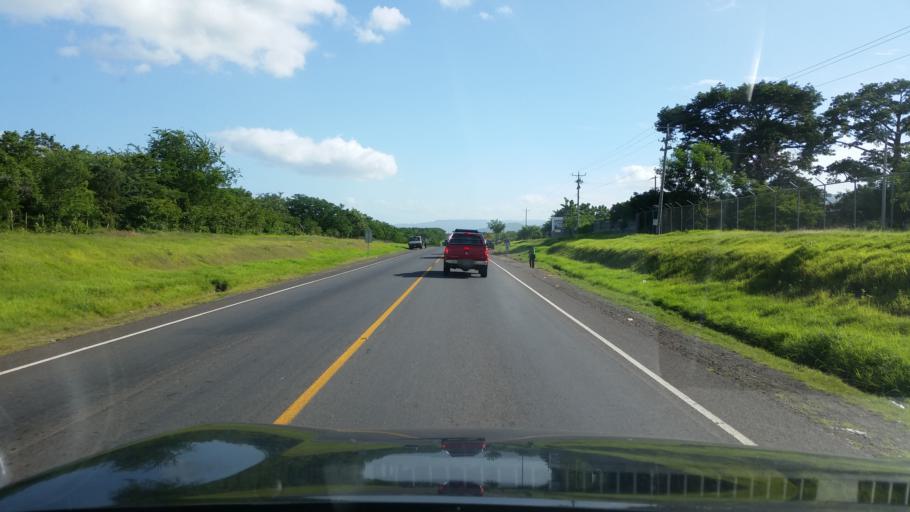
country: NI
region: Managua
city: Tipitapa
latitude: 12.3607
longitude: -86.0482
